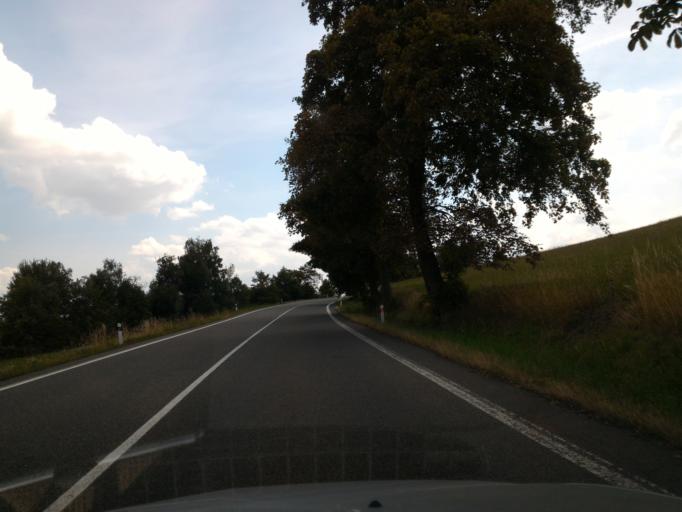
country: CZ
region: Vysocina
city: Bohdalov
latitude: 49.4722
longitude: 15.8256
